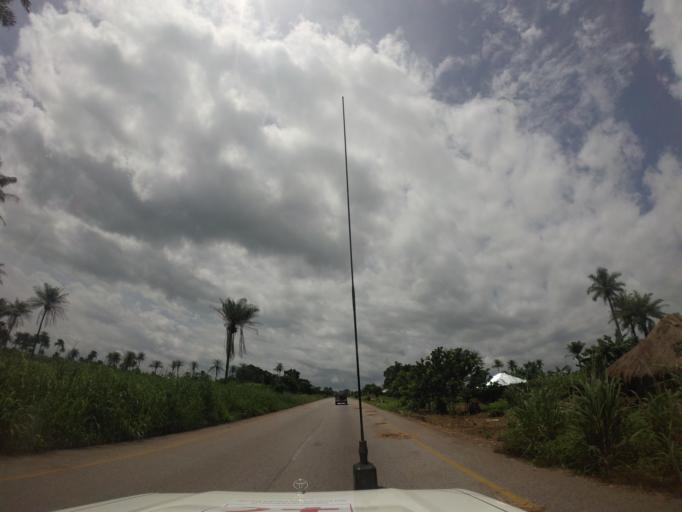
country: SL
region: Southern Province
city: Rotifunk
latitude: 8.4868
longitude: -12.7141
